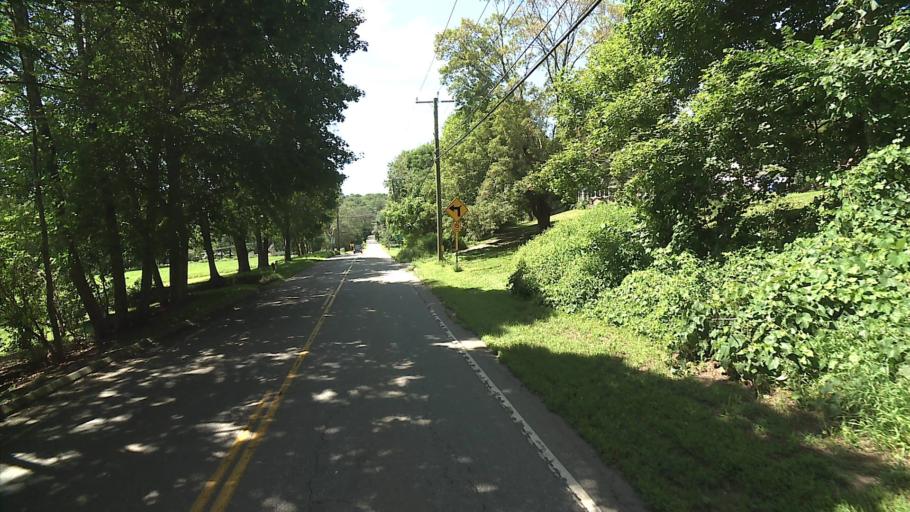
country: US
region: Connecticut
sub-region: Windham County
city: South Woodstock
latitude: 41.8953
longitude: -71.9739
